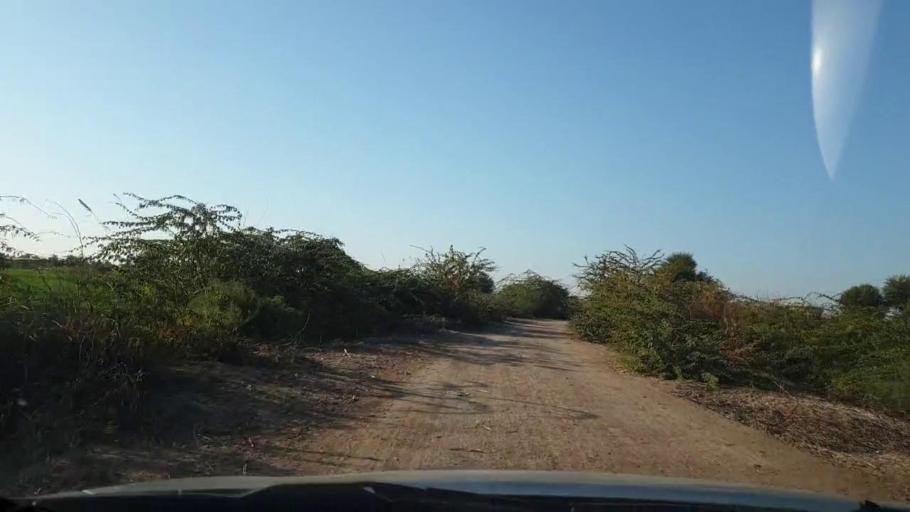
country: PK
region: Sindh
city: Jhol
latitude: 25.8999
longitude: 68.9254
